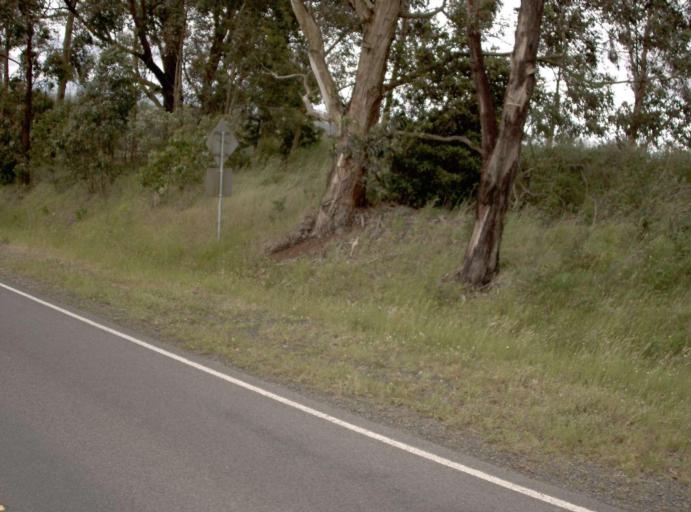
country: AU
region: Victoria
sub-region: Baw Baw
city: Warragul
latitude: -38.0611
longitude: 145.9674
